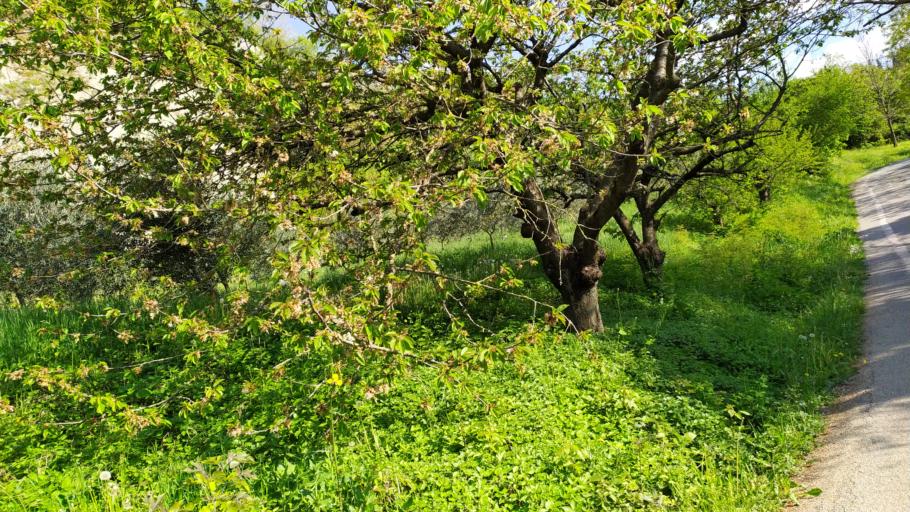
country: IT
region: Emilia-Romagna
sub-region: Provincia di Bologna
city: Borgo Tossignano
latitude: 44.2740
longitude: 11.6010
